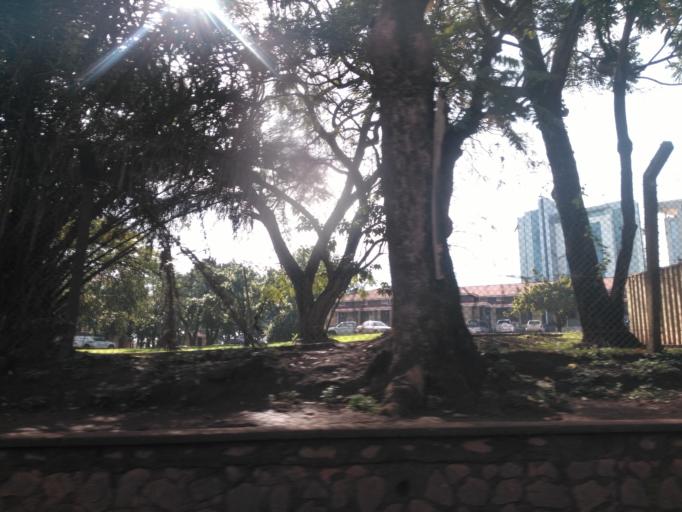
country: UG
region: Central Region
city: Kampala Central Division
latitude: 0.3329
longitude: 32.5765
